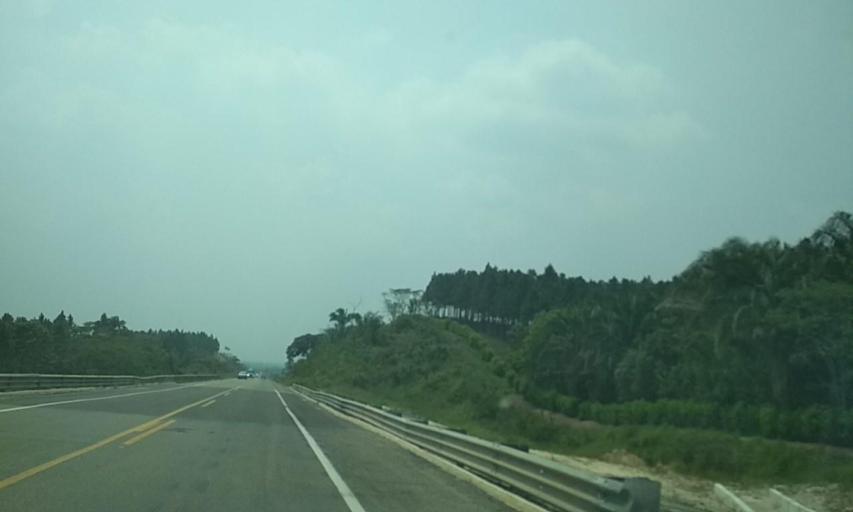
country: MX
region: Tabasco
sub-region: Huimanguillo
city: Francisco Rueda
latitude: 17.7506
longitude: -93.9951
